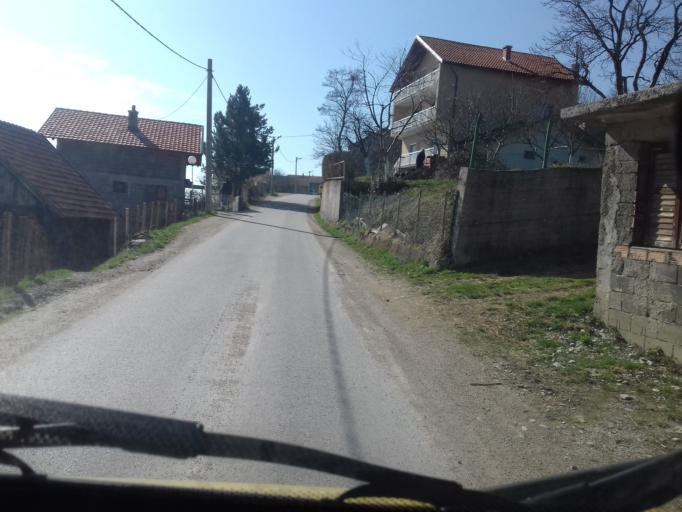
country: BA
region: Federation of Bosnia and Herzegovina
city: Travnik
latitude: 44.2529
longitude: 17.7346
